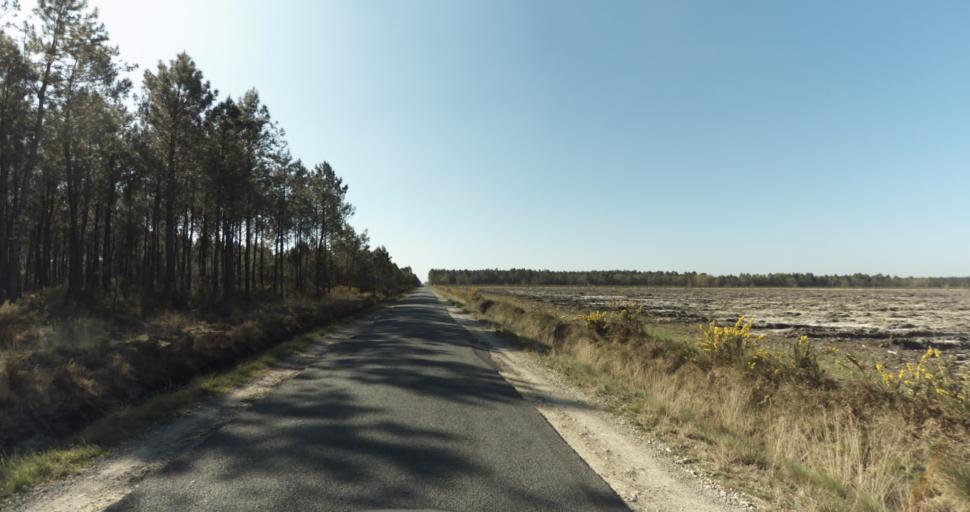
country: FR
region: Aquitaine
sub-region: Departement de la Gironde
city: Martignas-sur-Jalle
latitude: 44.7908
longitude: -0.8642
